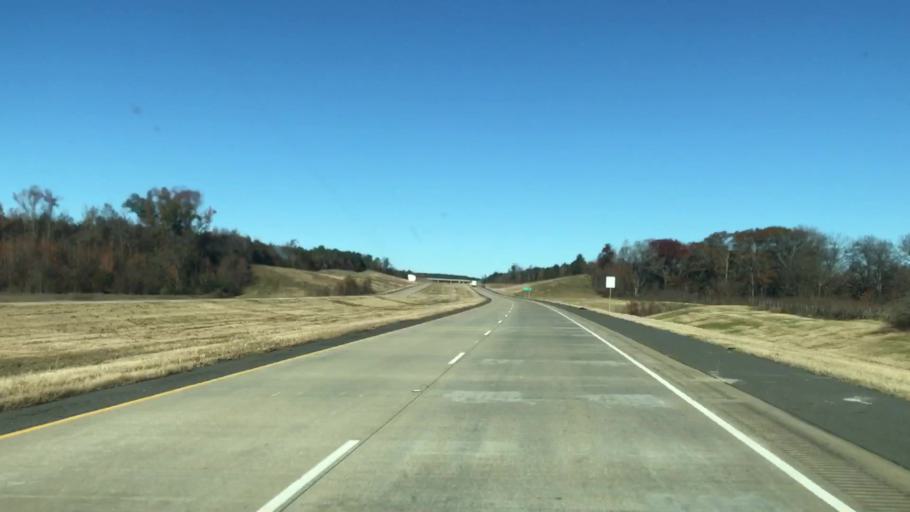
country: US
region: Louisiana
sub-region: Caddo Parish
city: Vivian
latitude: 32.9097
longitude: -93.8696
